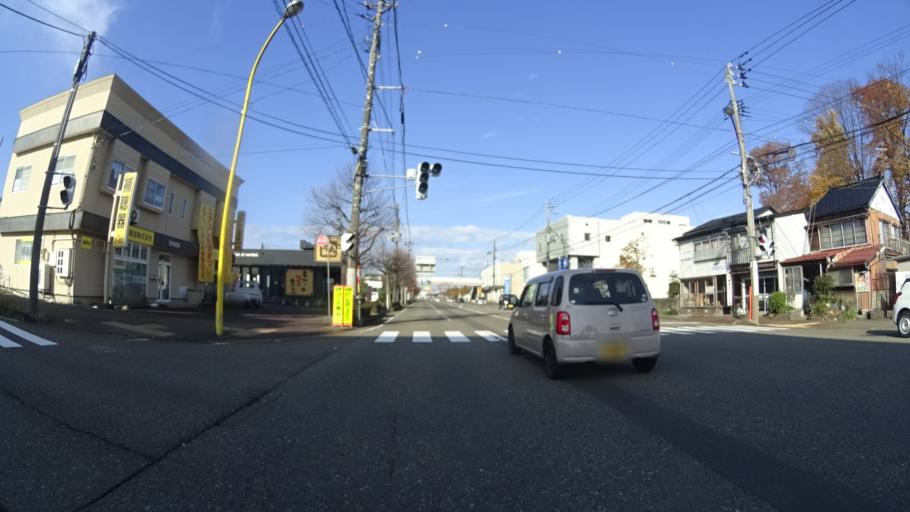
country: JP
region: Niigata
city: Joetsu
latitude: 37.1187
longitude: 138.2519
